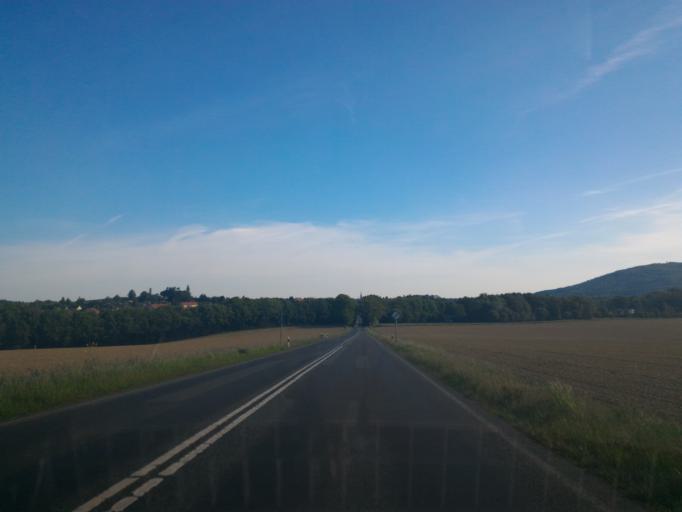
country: DE
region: Saxony
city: Grossschweidnitz
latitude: 51.0676
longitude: 14.6489
